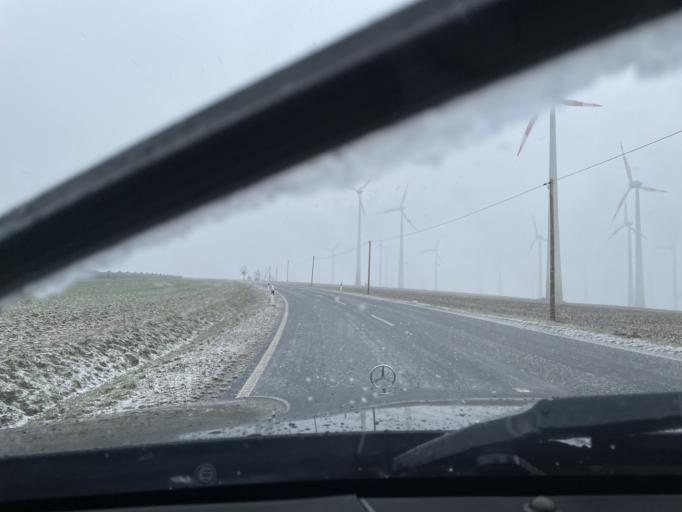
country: DE
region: Thuringia
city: Buttstedt
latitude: 51.2312
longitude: 10.2978
